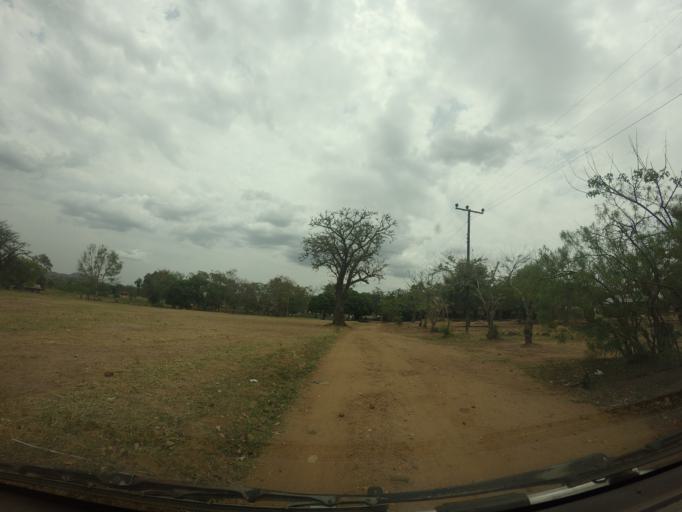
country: UG
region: Northern Region
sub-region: Arua District
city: Arua
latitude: 2.9449
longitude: 30.9399
